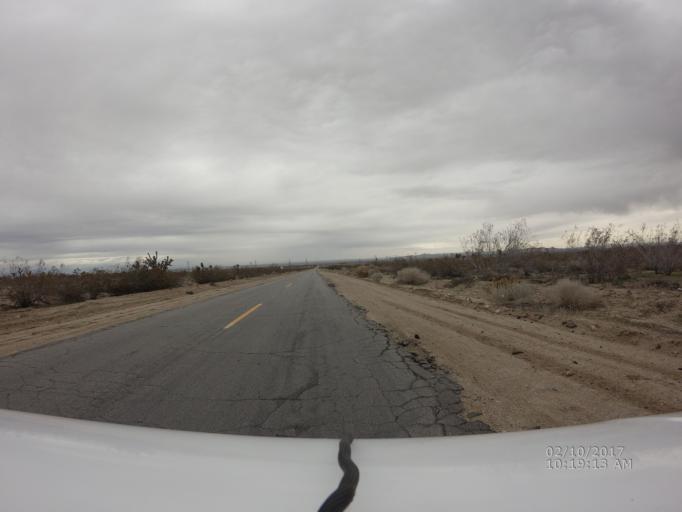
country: US
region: California
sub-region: Los Angeles County
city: Littlerock
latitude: 34.5017
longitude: -117.9579
